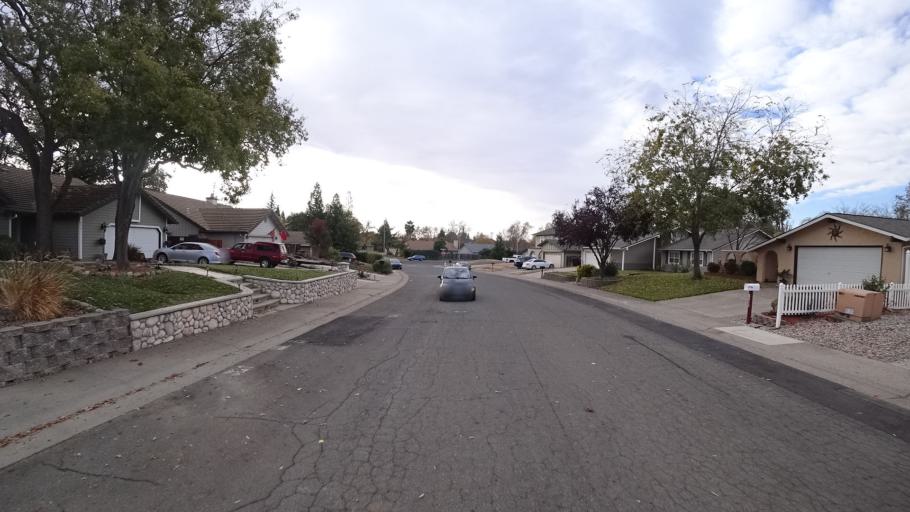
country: US
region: California
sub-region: Sacramento County
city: Citrus Heights
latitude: 38.7159
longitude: -121.2475
